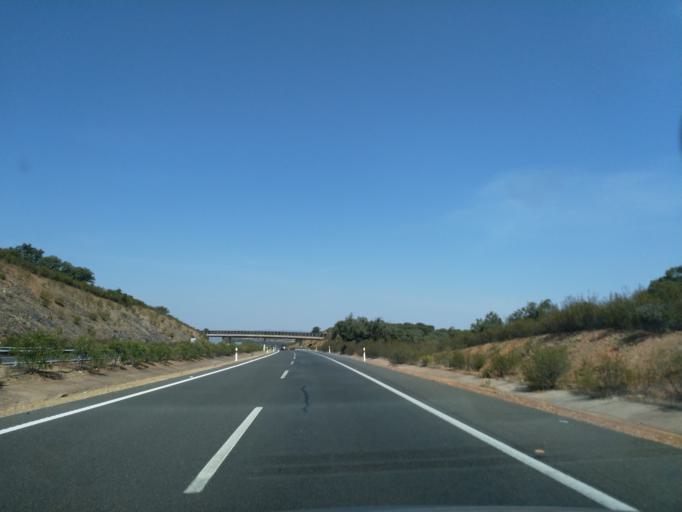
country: ES
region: Extremadura
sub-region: Provincia de Caceres
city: Alcuescar
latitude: 39.1741
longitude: -6.2711
